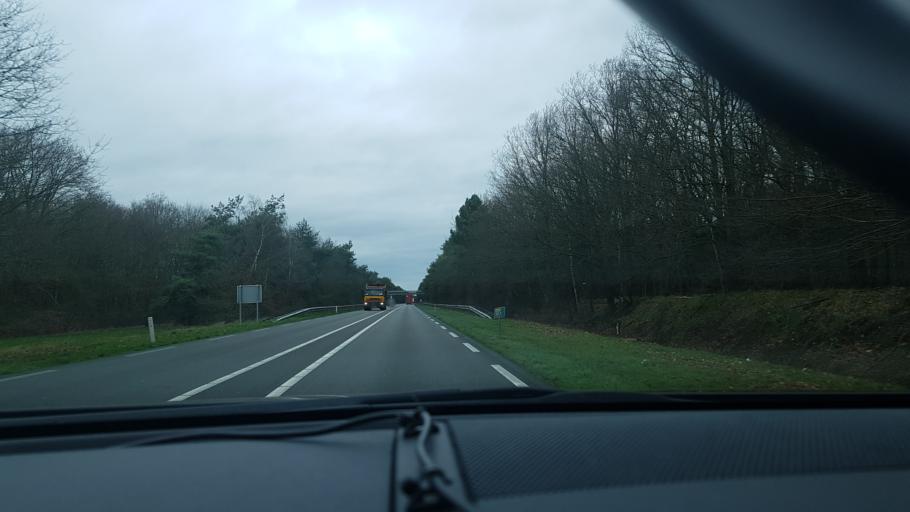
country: NL
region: North Brabant
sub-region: Gemeente Asten
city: Asten
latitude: 51.4405
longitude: 5.7332
